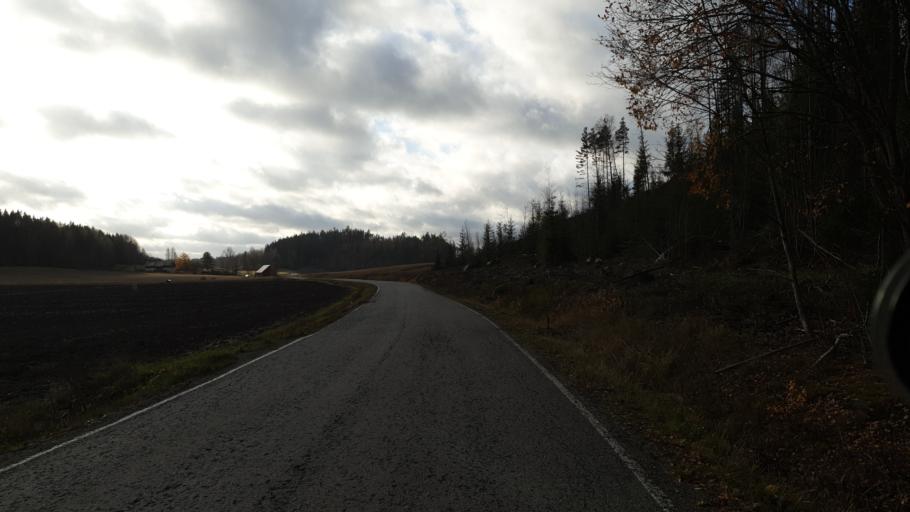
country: FI
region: Uusimaa
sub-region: Helsinki
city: Siuntio
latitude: 60.2584
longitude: 24.2992
